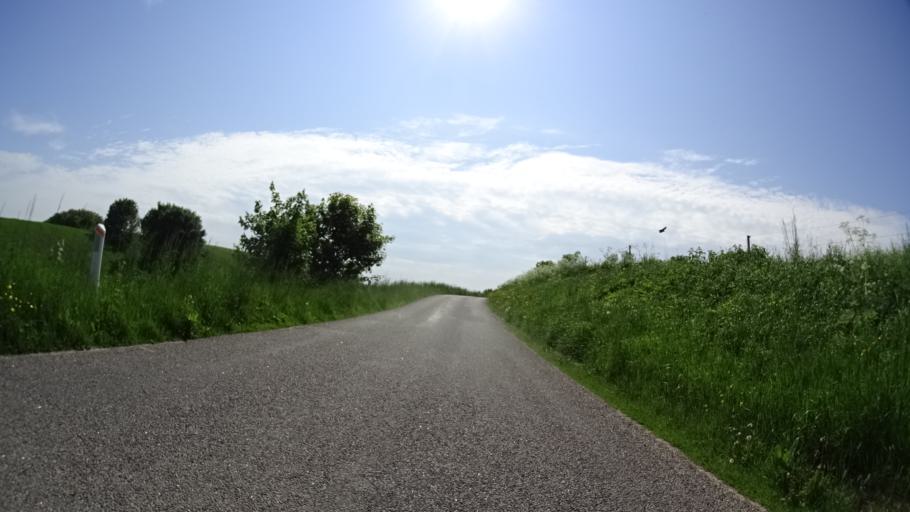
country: DK
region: Central Jutland
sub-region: Skanderborg Kommune
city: Horning
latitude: 56.0997
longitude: 10.0207
